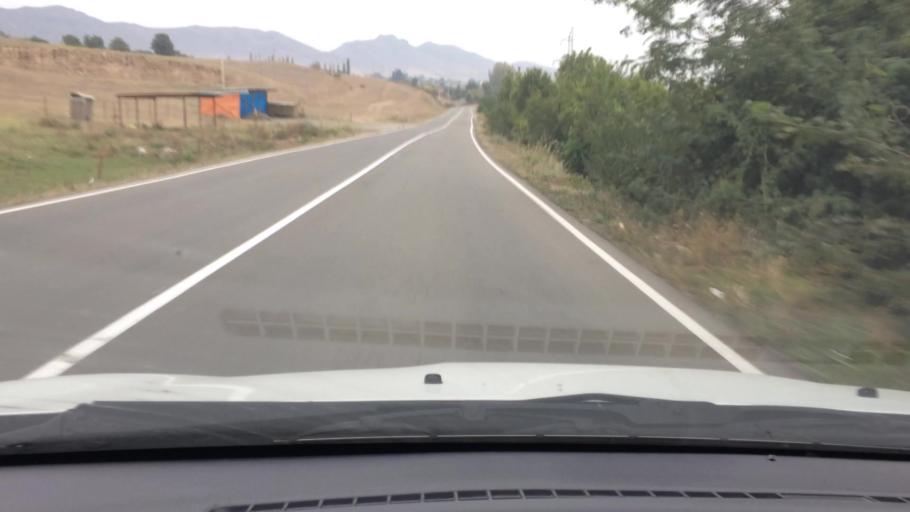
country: AM
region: Tavush
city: Bagratashen
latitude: 41.2867
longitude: 44.7896
